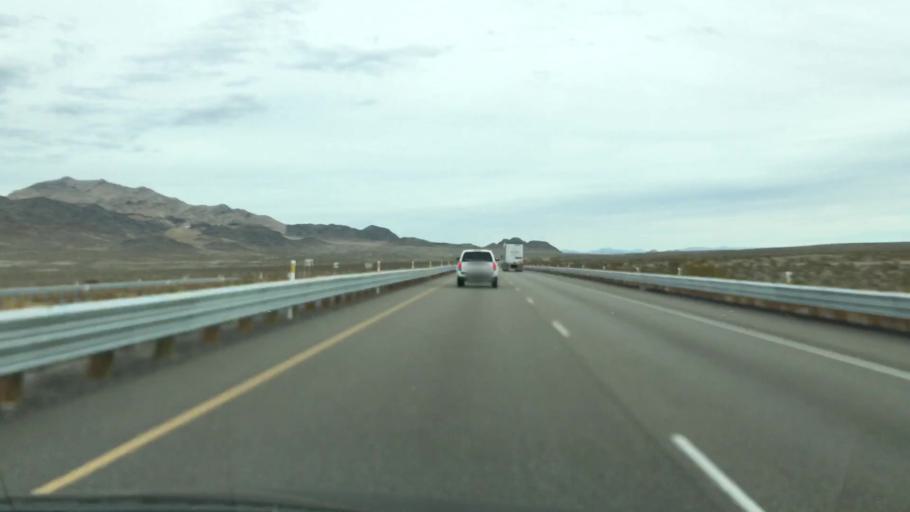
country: US
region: Nevada
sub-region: Nye County
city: Pahrump
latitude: 36.5981
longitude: -115.9966
